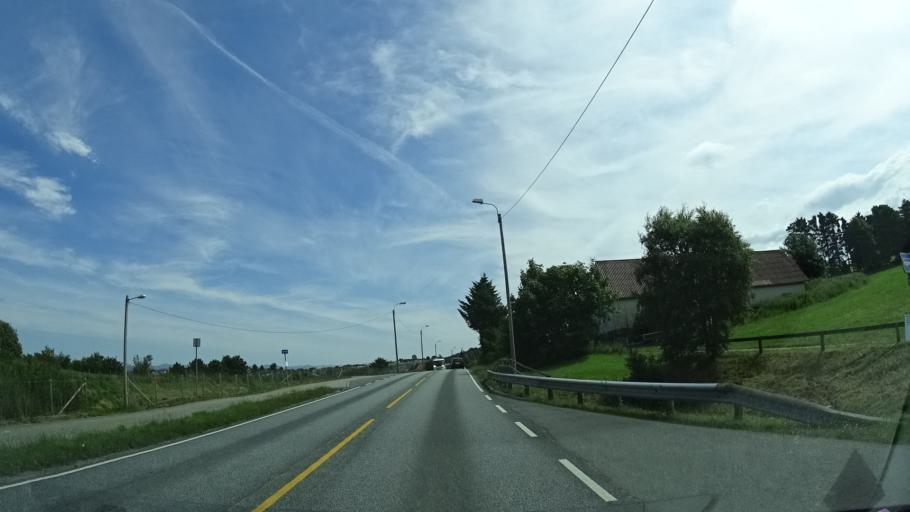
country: NO
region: Rogaland
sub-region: Randaberg
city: Randaberg
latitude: 58.9895
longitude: 5.6595
